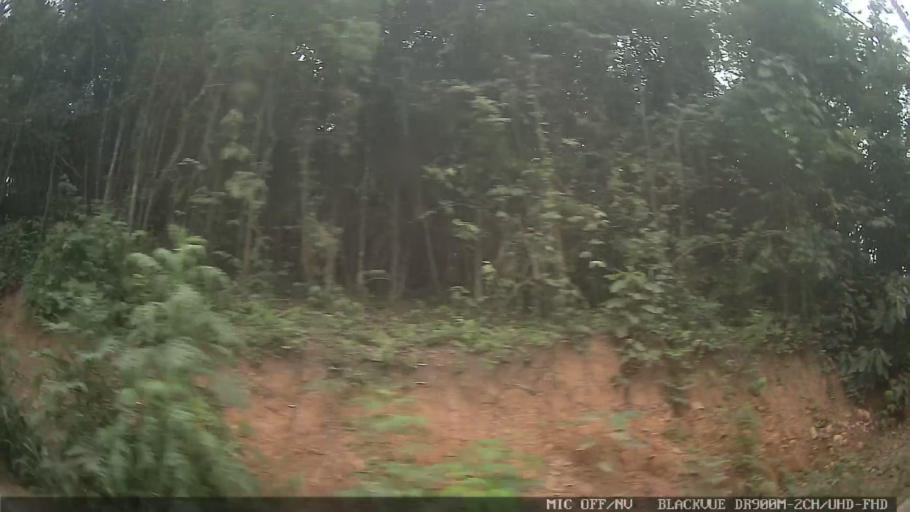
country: BR
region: Sao Paulo
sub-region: Atibaia
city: Atibaia
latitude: -23.1760
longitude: -46.6222
